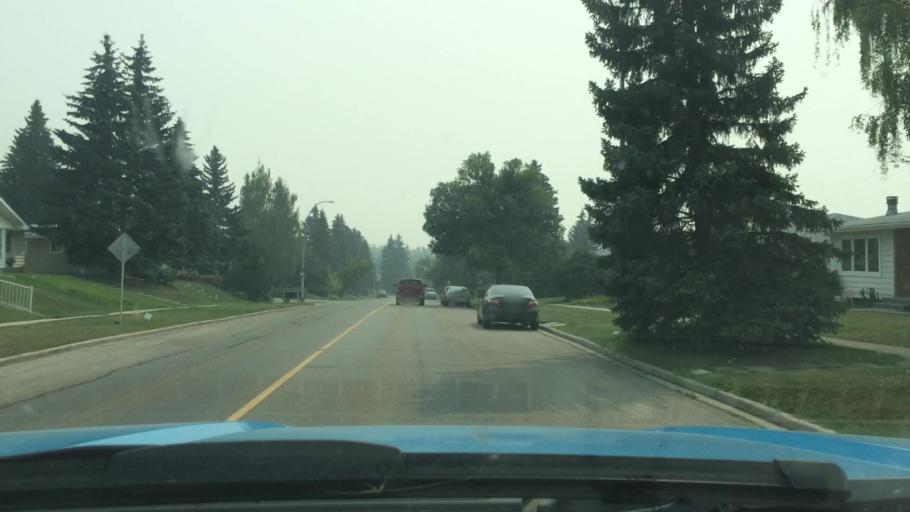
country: CA
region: Alberta
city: Calgary
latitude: 51.0986
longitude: -114.1279
